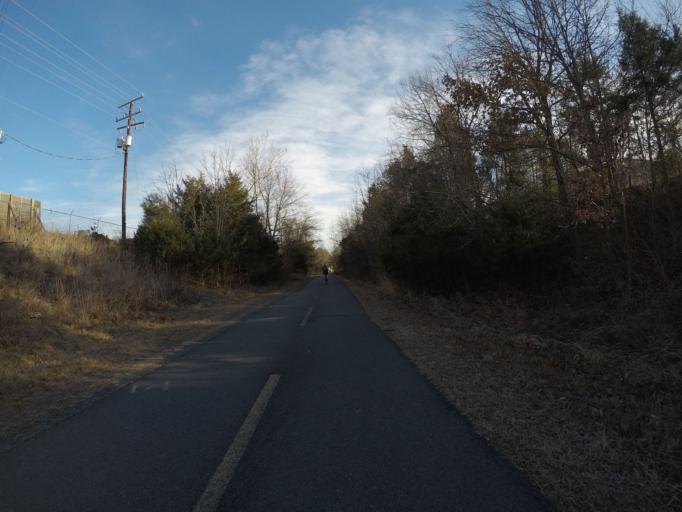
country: US
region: Virginia
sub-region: Loudoun County
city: Leesburg
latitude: 39.1012
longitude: -77.5480
